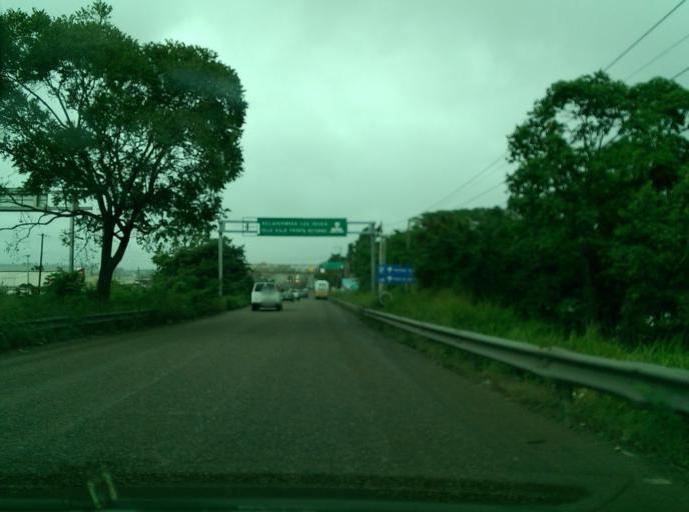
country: MX
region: Tabasco
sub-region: Nacajuca
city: Brisas del Carrizal
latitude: 17.9883
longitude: -92.9715
